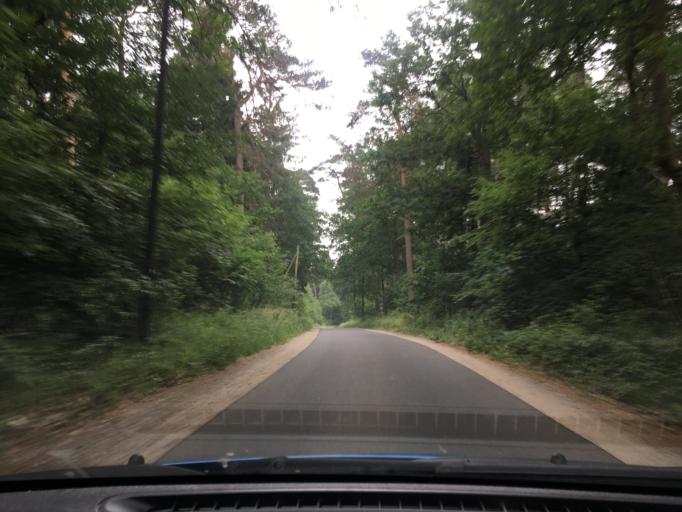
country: DE
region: Lower Saxony
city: Zernien
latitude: 53.1029
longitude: 10.8905
